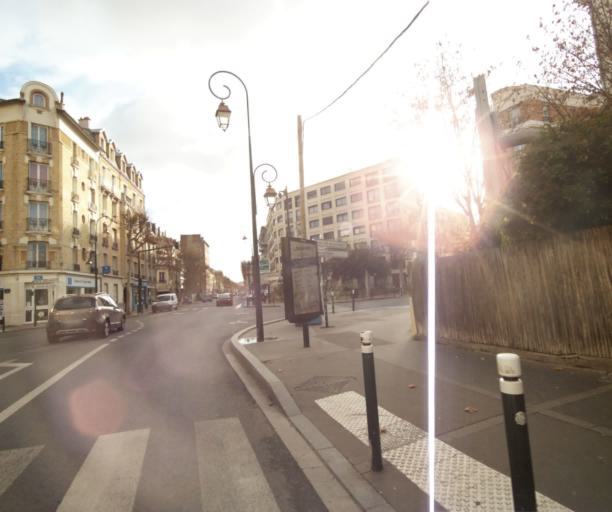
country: FR
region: Ile-de-France
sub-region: Departement des Hauts-de-Seine
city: Colombes
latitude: 48.9114
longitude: 2.2545
